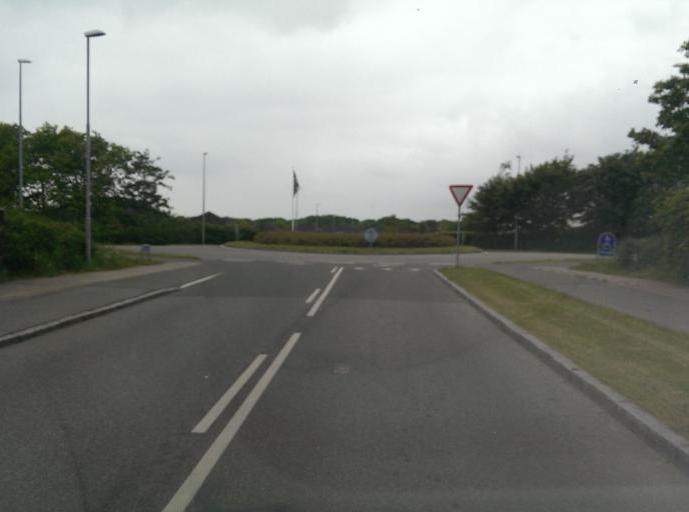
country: DK
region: South Denmark
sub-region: Fano Kommune
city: Nordby
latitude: 55.5326
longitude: 8.3619
